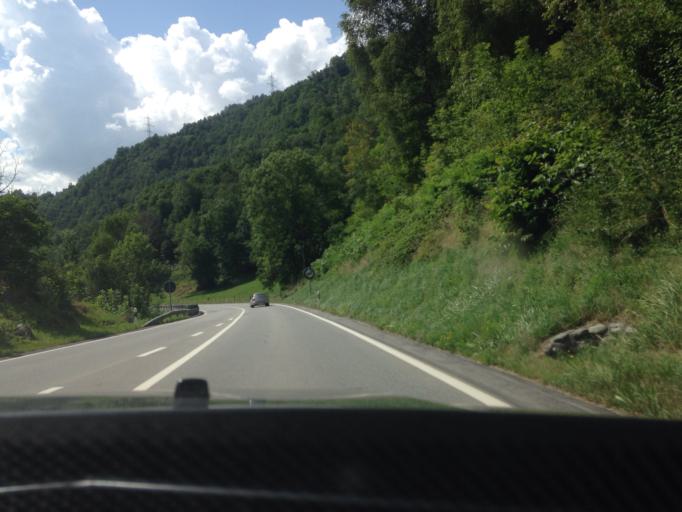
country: CH
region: Grisons
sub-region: Surselva District
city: Breil
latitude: 46.7569
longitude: 9.0662
